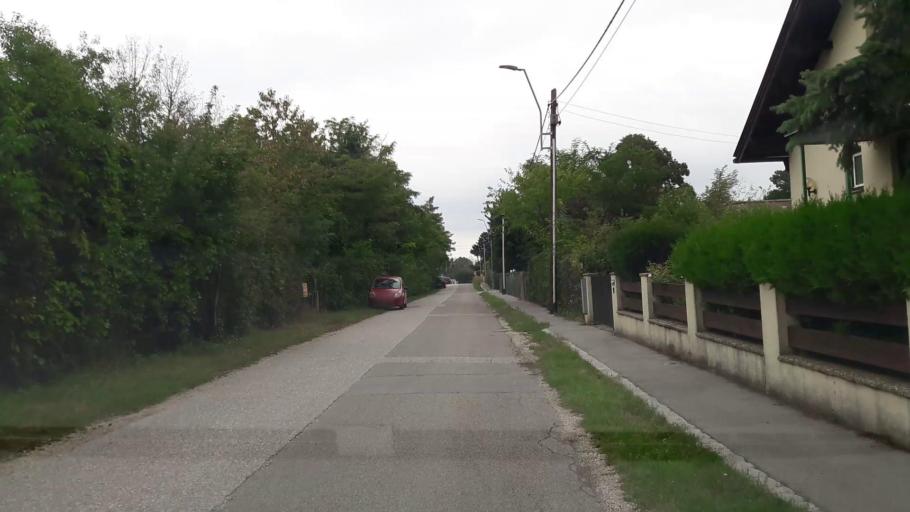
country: AT
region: Lower Austria
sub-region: Politischer Bezirk Ganserndorf
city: Strasshof an der Nordbahn
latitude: 48.3244
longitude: 16.6761
